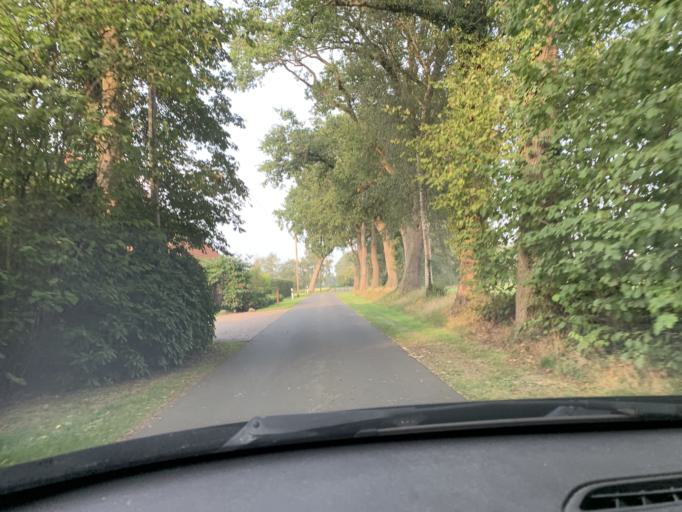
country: DE
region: Lower Saxony
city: Apen
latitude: 53.2475
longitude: 7.8300
